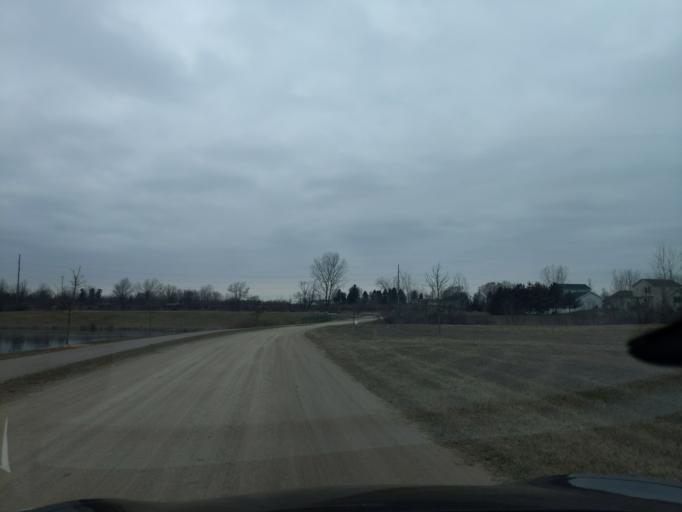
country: US
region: Michigan
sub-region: Eaton County
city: Potterville
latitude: 42.6214
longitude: -84.7534
